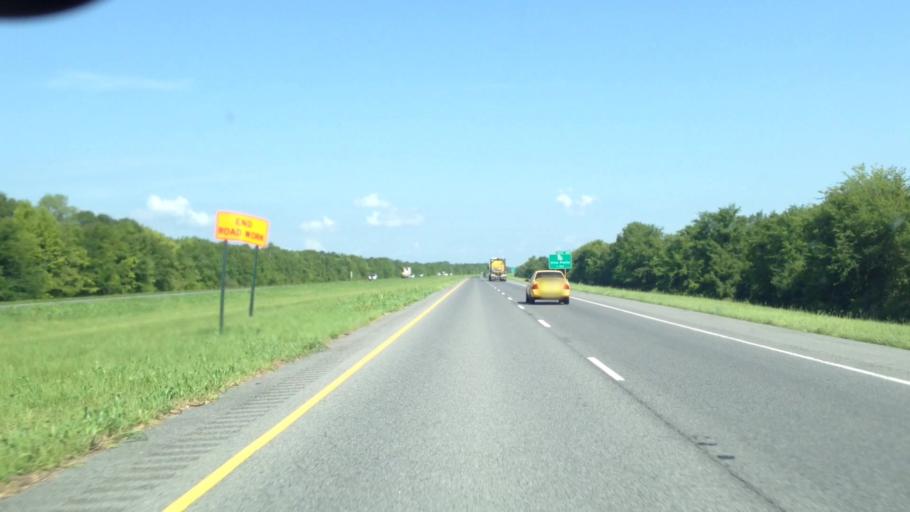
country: US
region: Louisiana
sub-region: Evangeline Parish
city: Ville Platte
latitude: 30.7648
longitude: -92.1726
